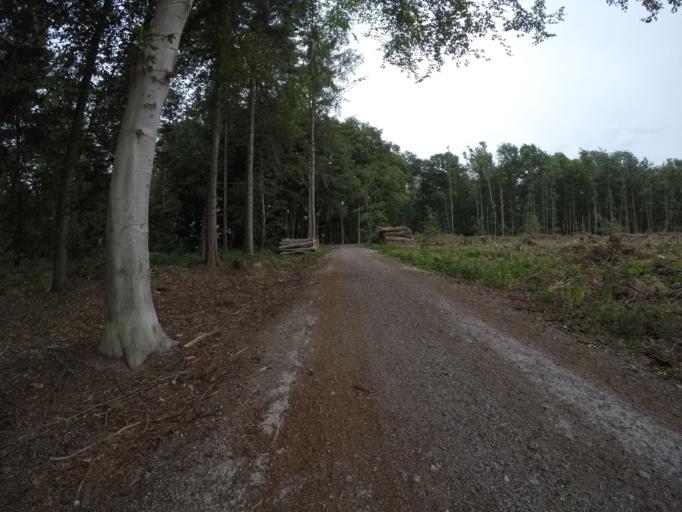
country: NL
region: Gelderland
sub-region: Oude IJsselstreek
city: Gendringen
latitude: 51.8583
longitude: 6.4224
